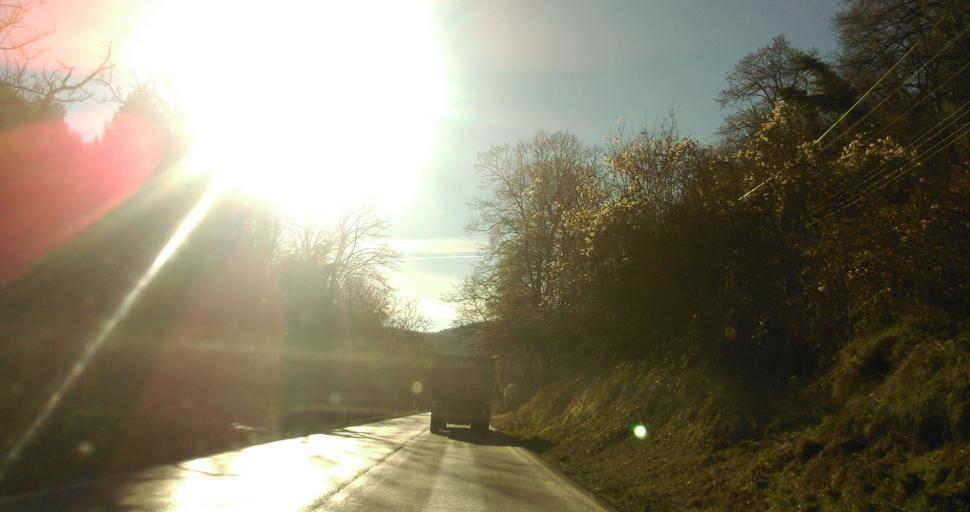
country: RS
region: Autonomna Pokrajina Vojvodina
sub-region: Juznobacki Okrug
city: Novi Sad
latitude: 45.1852
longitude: 19.8398
